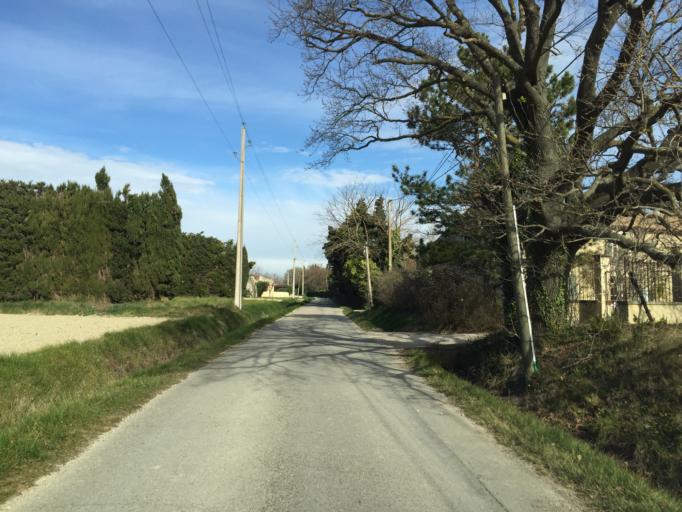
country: FR
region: Provence-Alpes-Cote d'Azur
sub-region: Departement du Vaucluse
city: Caderousse
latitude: 44.1192
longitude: 4.7424
